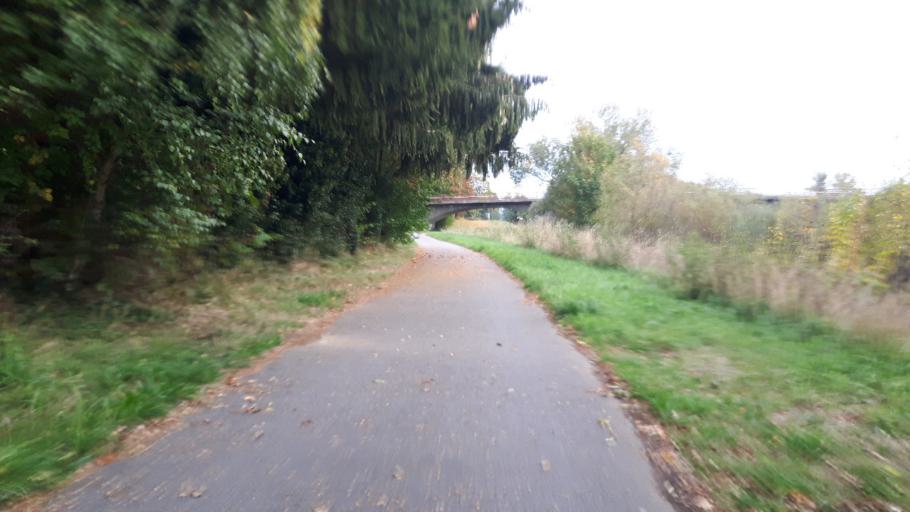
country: DE
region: North Rhine-Westphalia
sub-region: Regierungsbezirk Koln
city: Eitorf
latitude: 50.7769
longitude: 7.4490
